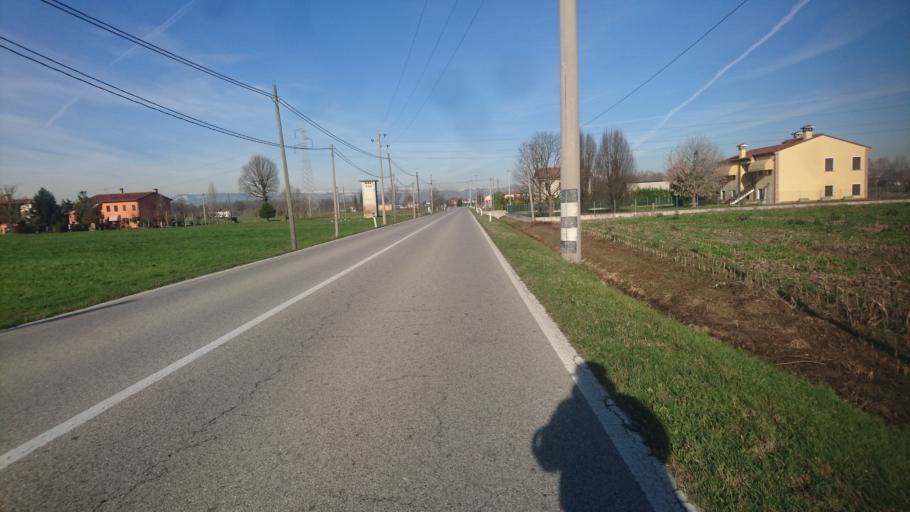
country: IT
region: Veneto
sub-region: Provincia di Padova
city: Tremignon
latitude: 45.5150
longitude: 11.7860
